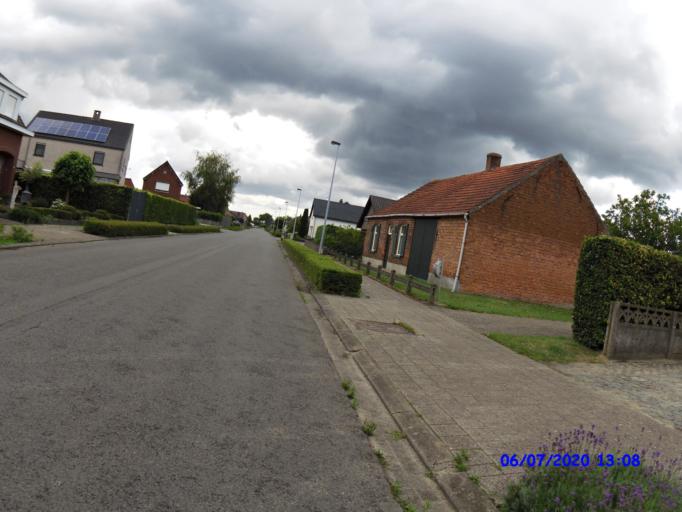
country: BE
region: Flanders
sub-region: Provincie Antwerpen
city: Dessel
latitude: 51.2382
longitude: 5.1352
